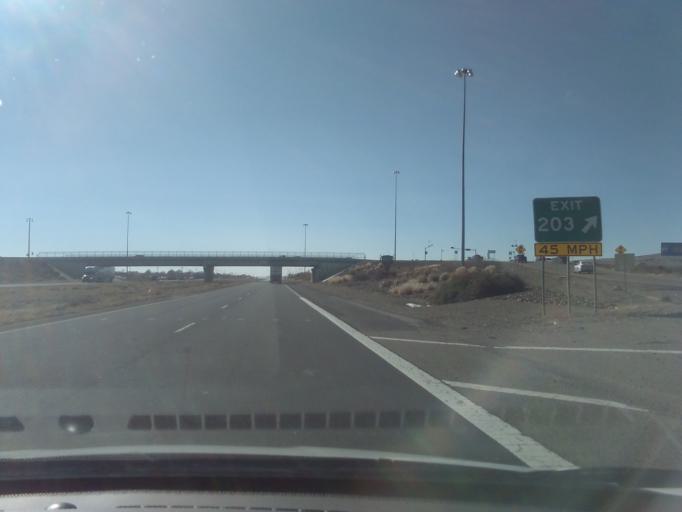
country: US
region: New Mexico
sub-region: Valencia County
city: Los Lunas
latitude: 34.8163
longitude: -106.7606
